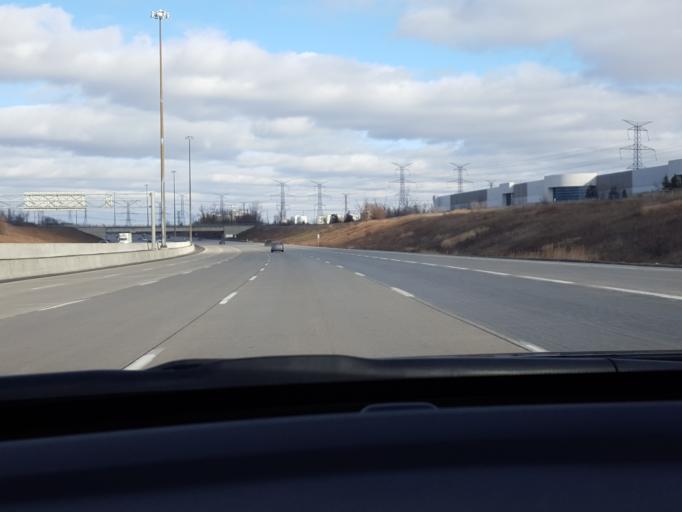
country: CA
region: Ontario
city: Concord
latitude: 43.7938
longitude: -79.4925
